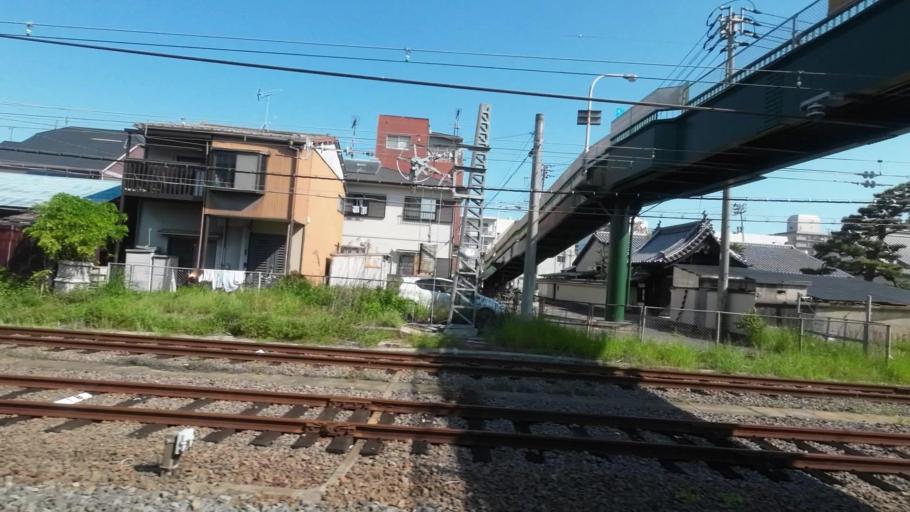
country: JP
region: Kagawa
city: Takamatsu-shi
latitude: 34.3485
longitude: 134.0385
